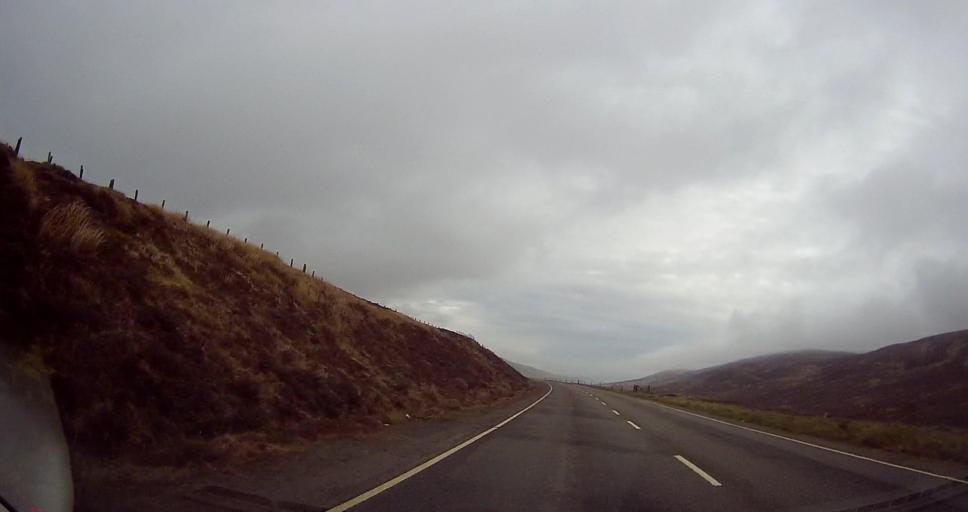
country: GB
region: Scotland
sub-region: Shetland Islands
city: Lerwick
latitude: 60.1464
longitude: -1.2405
